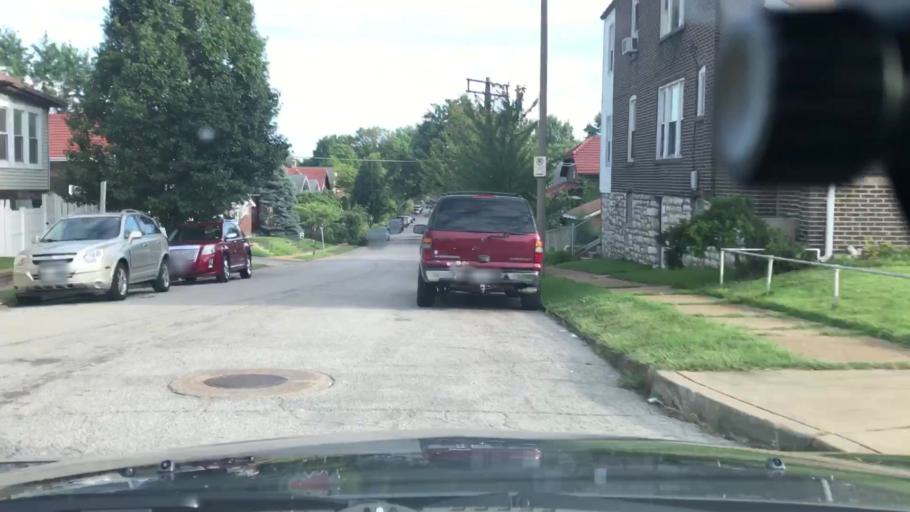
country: US
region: Missouri
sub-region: Saint Louis County
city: Lemay
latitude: 38.5793
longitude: -90.2810
